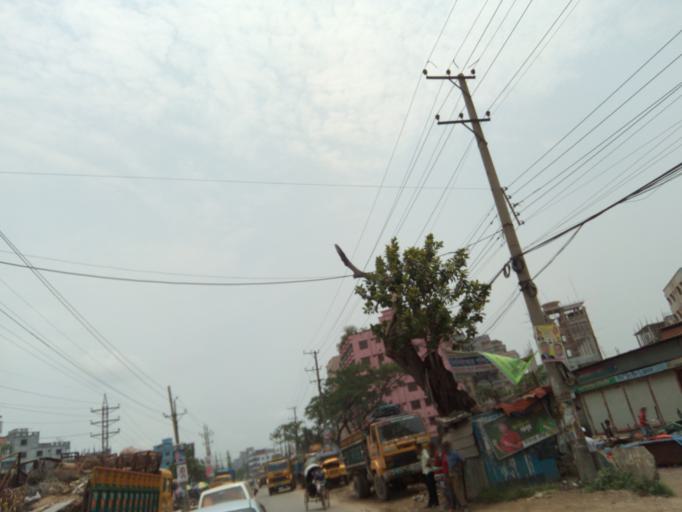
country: BD
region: Dhaka
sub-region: Dhaka
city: Dhaka
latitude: 23.6891
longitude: 90.4323
